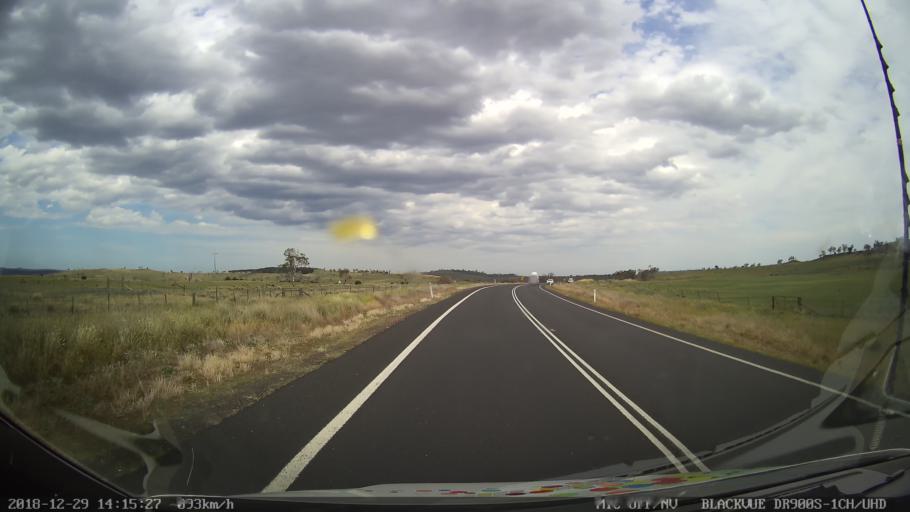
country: AU
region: New South Wales
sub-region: Cooma-Monaro
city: Cooma
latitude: -36.4557
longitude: 149.2411
